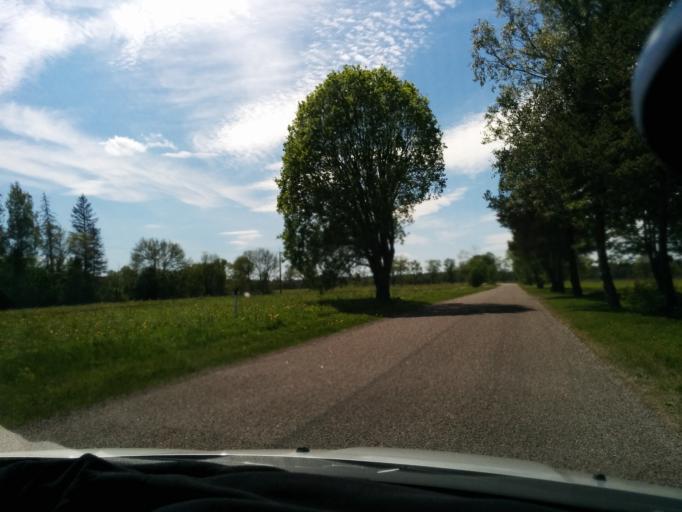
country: EE
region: Harju
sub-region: Loksa linn
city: Loksa
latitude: 59.5193
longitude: 25.9472
